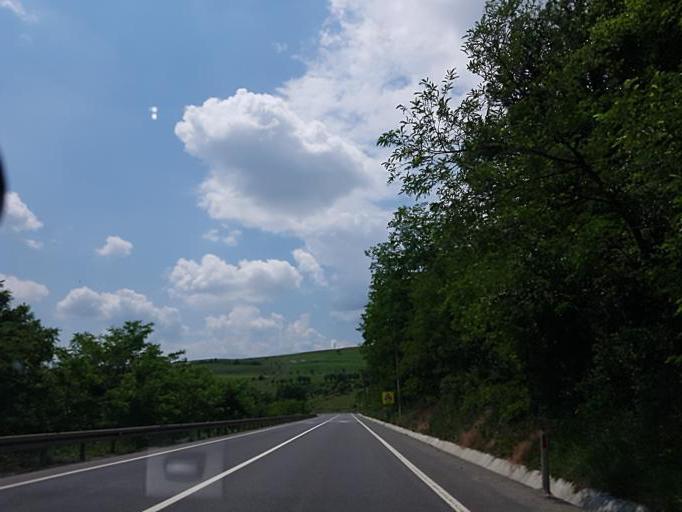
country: RO
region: Sibiu
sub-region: Comuna Slimnic
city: Slimnic
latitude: 45.9339
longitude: 24.1705
